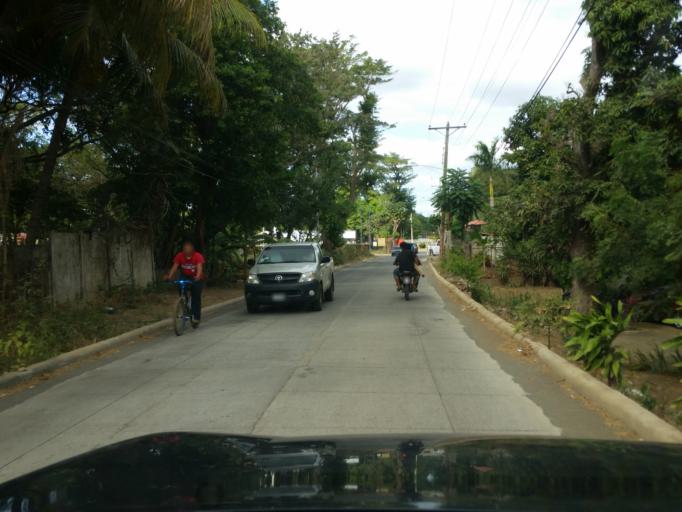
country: NI
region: Managua
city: Managua
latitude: 12.0776
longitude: -86.2283
